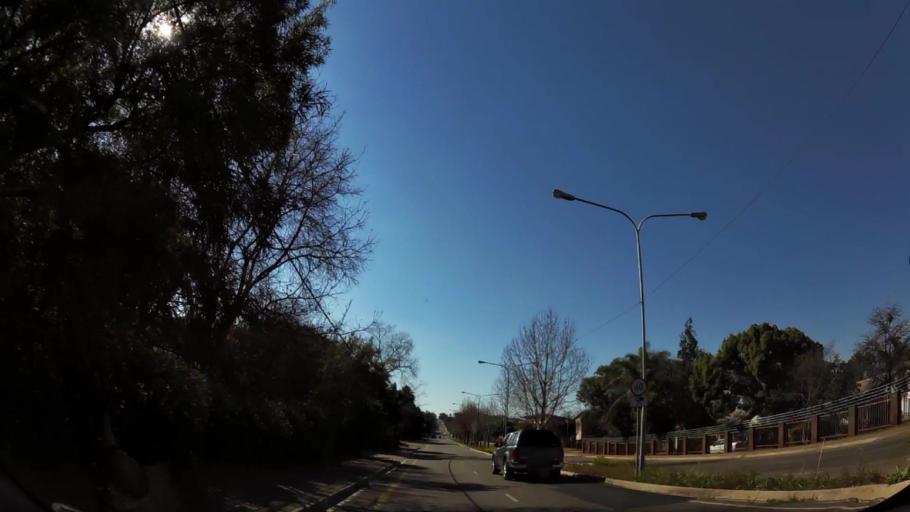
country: ZA
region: Gauteng
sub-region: City of Tshwane Metropolitan Municipality
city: Centurion
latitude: -25.8420
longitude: 28.2078
